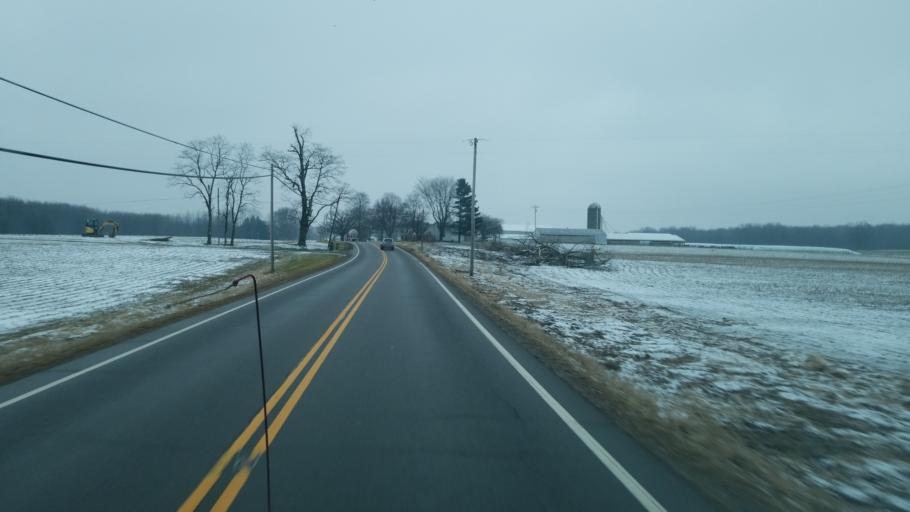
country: US
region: Ohio
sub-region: Wayne County
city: Shreve
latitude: 40.7665
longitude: -82.0440
